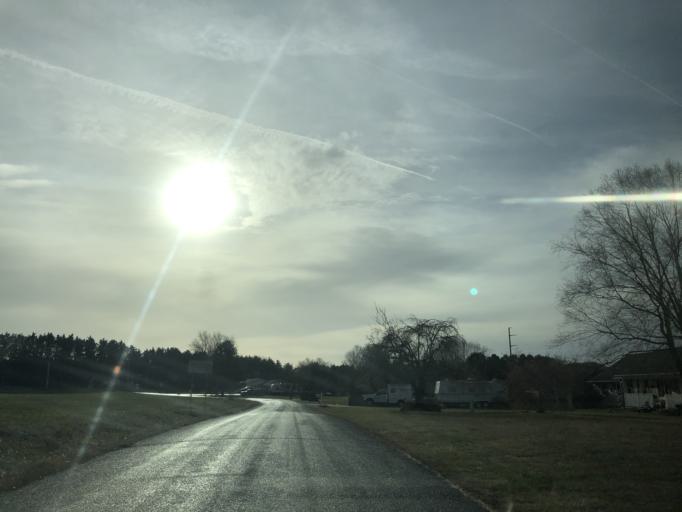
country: US
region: Delaware
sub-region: New Castle County
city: Townsend
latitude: 39.4507
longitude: -75.6317
